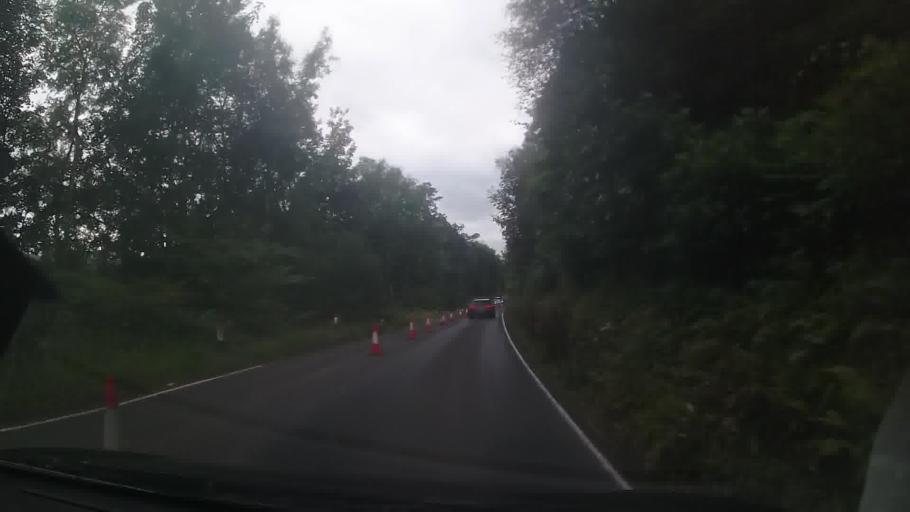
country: GB
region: Scotland
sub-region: Argyll and Bute
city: Garelochhead
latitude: 56.2364
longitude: -5.0790
